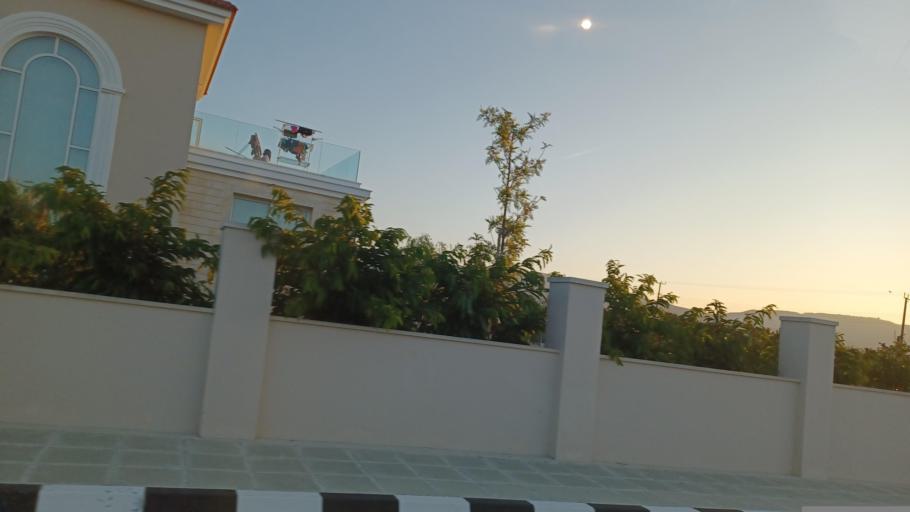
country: CY
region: Pafos
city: Pegeia
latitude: 34.8656
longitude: 32.3593
